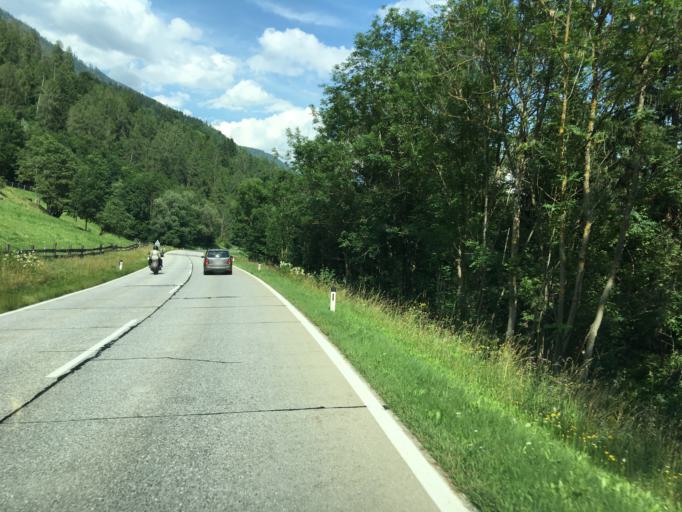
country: AT
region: Carinthia
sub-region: Politischer Bezirk Spittal an der Drau
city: Flattach
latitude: 46.9346
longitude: 13.0956
